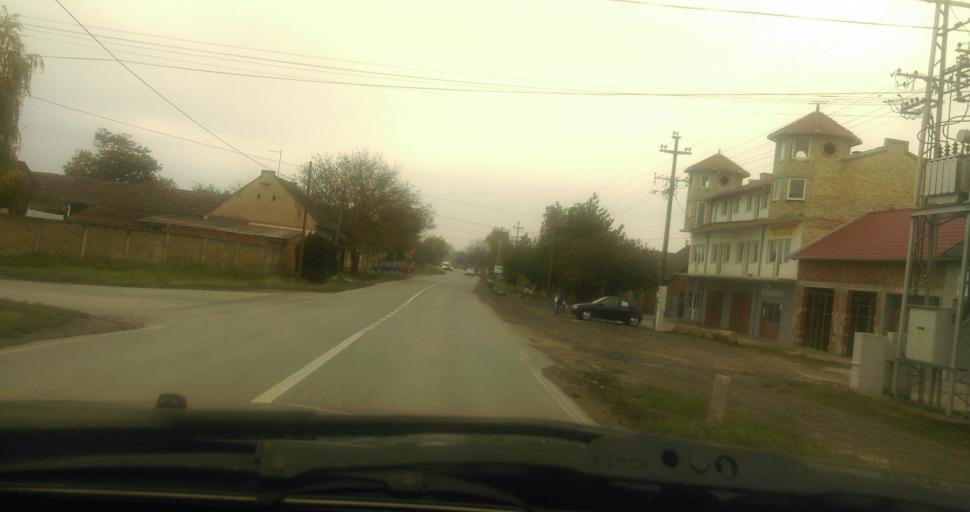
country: RS
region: Autonomna Pokrajina Vojvodina
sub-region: Juznobacki Okrug
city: Becej
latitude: 45.6034
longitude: 20.0379
